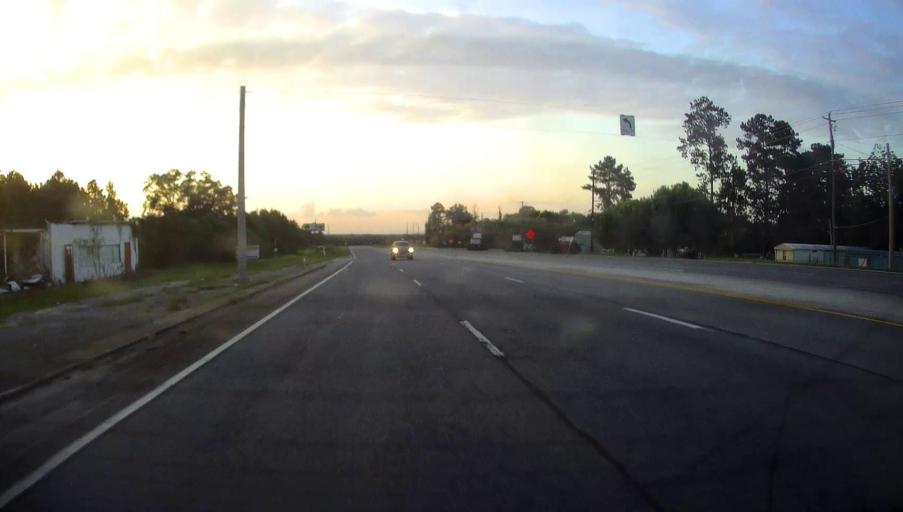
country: US
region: Georgia
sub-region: Bibb County
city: Macon
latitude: 32.7500
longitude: -83.6574
